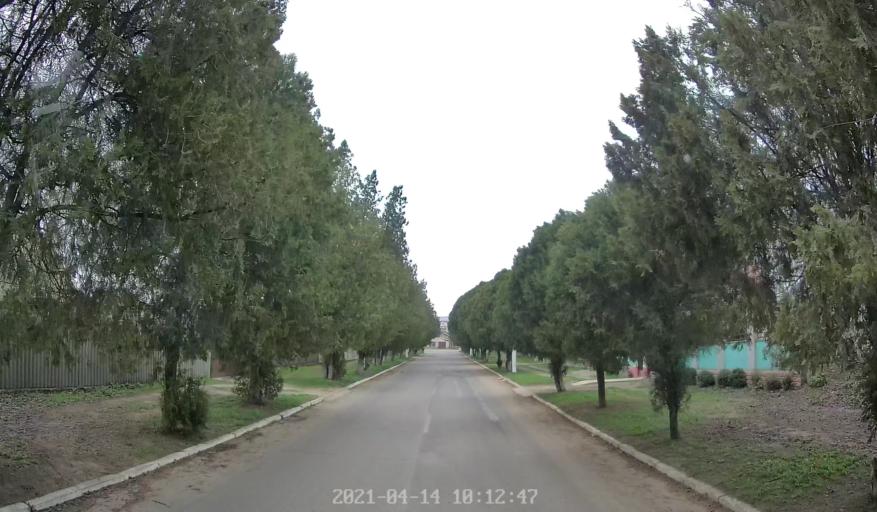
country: MD
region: Criuleni
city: Criuleni
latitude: 47.1475
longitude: 29.1321
